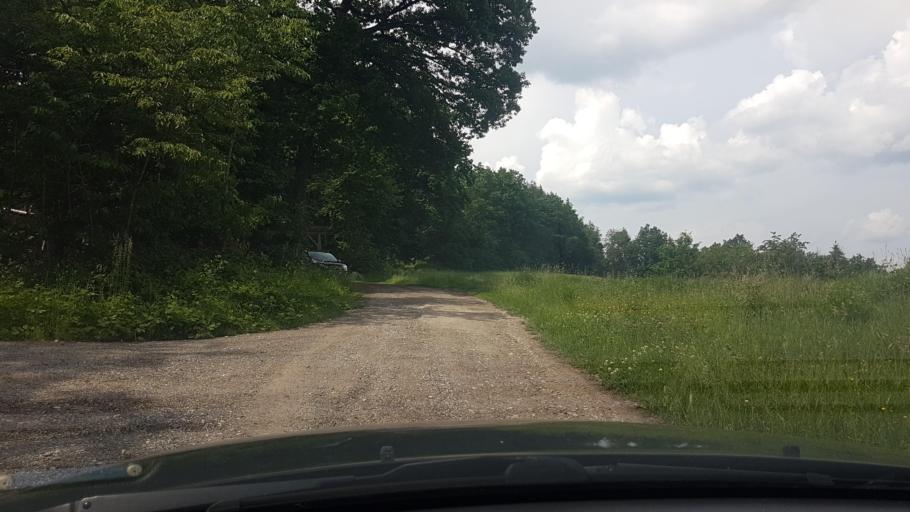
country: DE
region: Bavaria
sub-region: Upper Franconia
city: Bischberg
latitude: 49.9042
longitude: 10.8093
